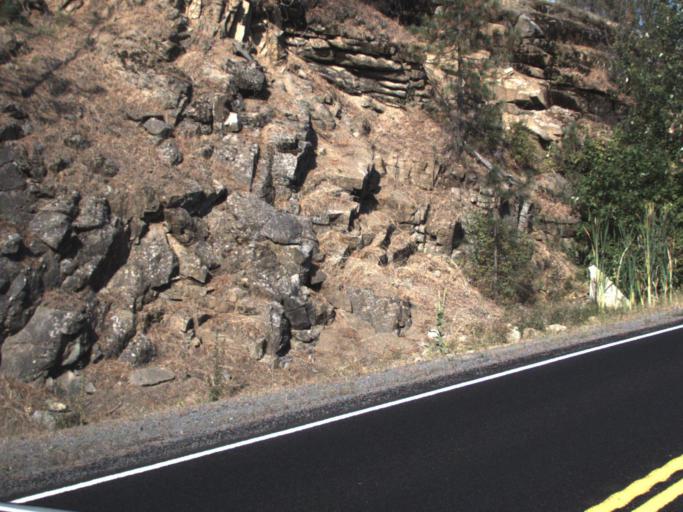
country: US
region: Washington
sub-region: Spokane County
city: Deer Park
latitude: 47.8780
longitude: -117.7048
